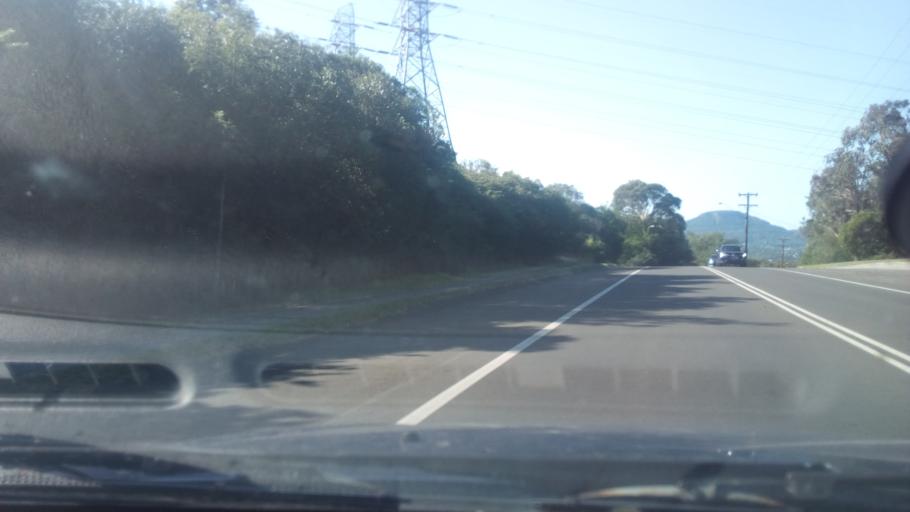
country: AU
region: New South Wales
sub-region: Wollongong
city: Berkeley
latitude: -34.4696
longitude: 150.8523
